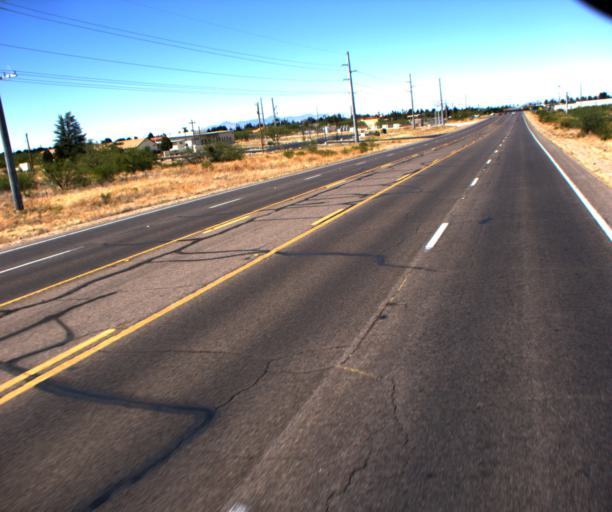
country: US
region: Arizona
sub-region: Cochise County
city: Sierra Vista Southeast
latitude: 31.4630
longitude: -110.2574
